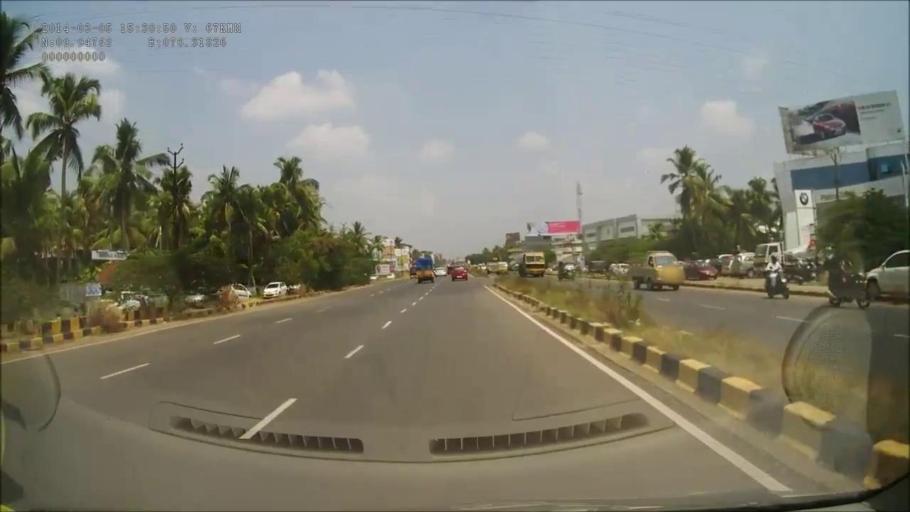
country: IN
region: Kerala
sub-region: Ernakulam
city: Cochin
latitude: 9.9484
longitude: 76.3183
